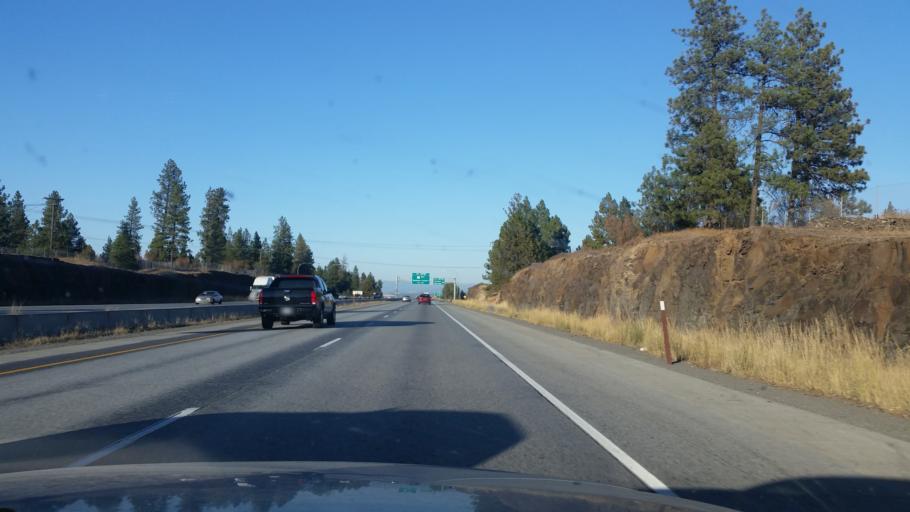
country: US
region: Washington
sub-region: Spokane County
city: Spokane
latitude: 47.6274
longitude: -117.4901
